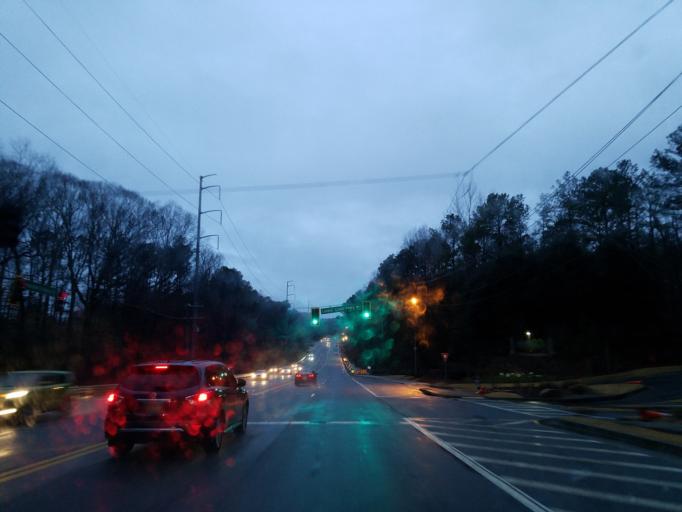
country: US
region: Georgia
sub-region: Fulton County
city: Roswell
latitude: 34.0122
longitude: -84.3039
